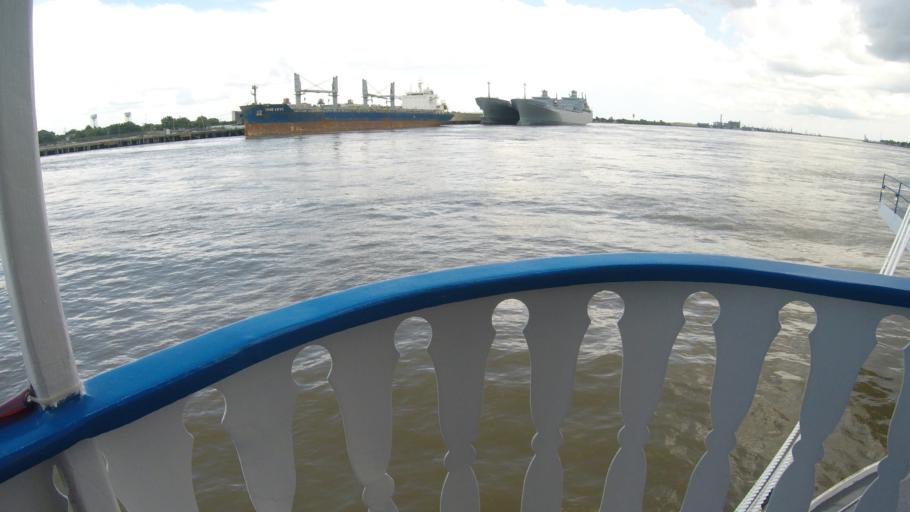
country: US
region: Louisiana
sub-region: Saint Bernard Parish
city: Arabi
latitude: 29.9578
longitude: -90.0384
